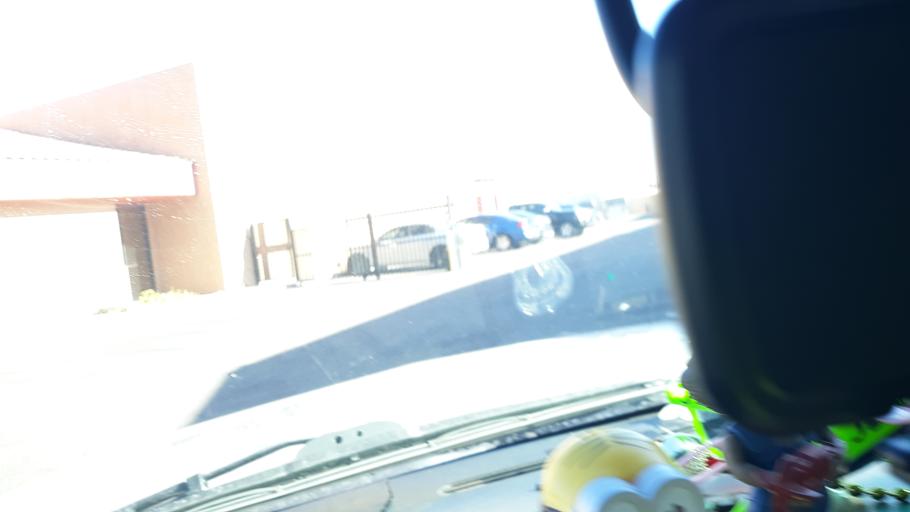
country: US
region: Arizona
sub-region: Maricopa County
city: Glendale
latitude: 33.5101
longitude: -112.1731
